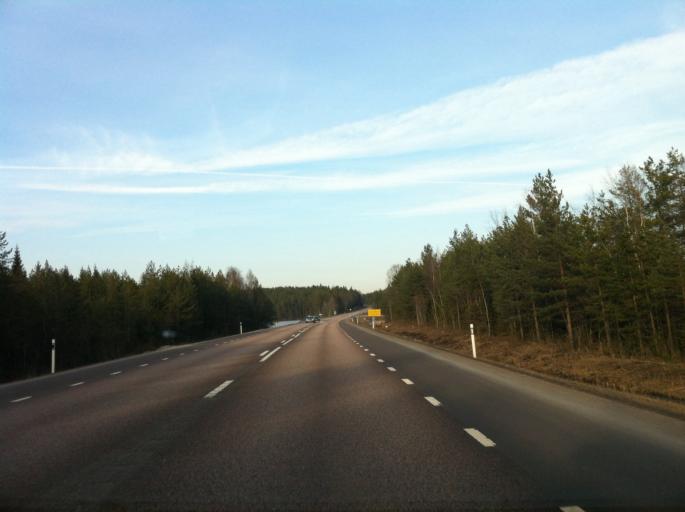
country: SE
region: Vaermland
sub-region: Filipstads Kommun
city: Filipstad
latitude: 59.7335
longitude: 14.2207
